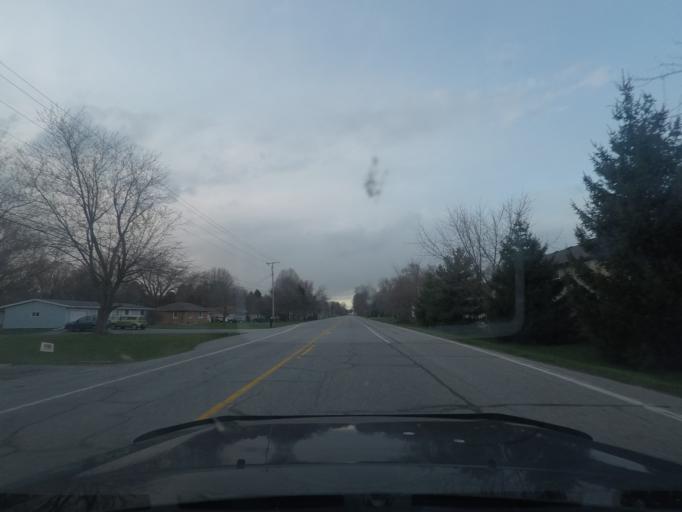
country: US
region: Indiana
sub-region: LaPorte County
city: LaPorte
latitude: 41.5917
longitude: -86.7391
